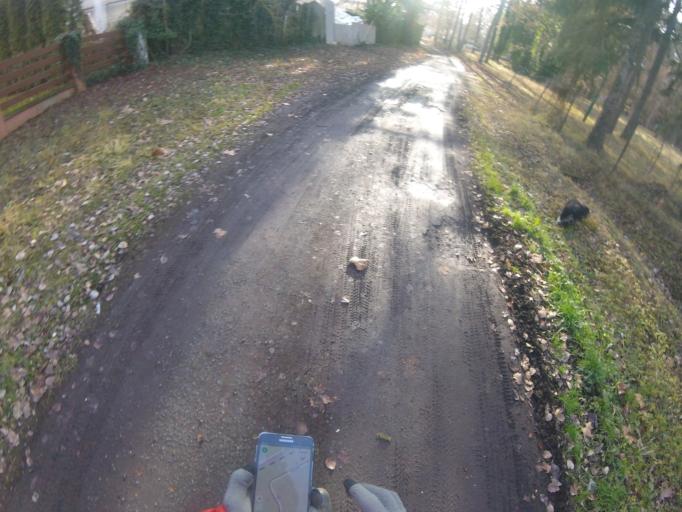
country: HU
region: Somogy
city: Balatonfoldvar
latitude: 46.8509
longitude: 17.8769
